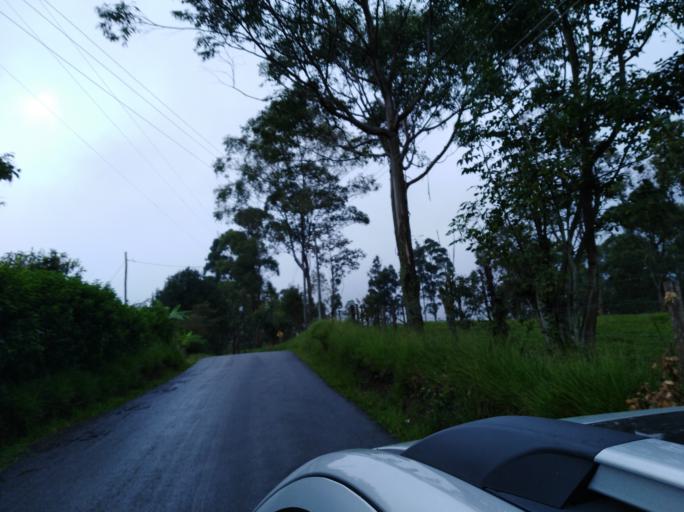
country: CO
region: Cauca
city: Cajibio
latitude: 2.6041
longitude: -76.5341
